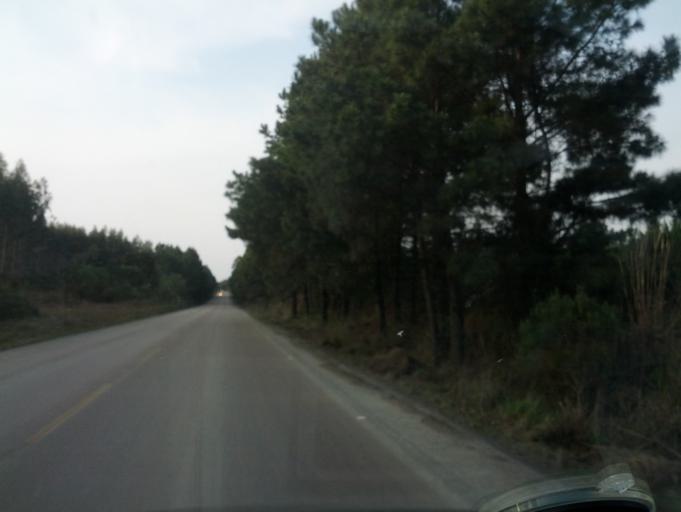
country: BR
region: Santa Catarina
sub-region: Otacilio Costa
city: Otacilio Costa
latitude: -27.4388
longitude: -50.1246
